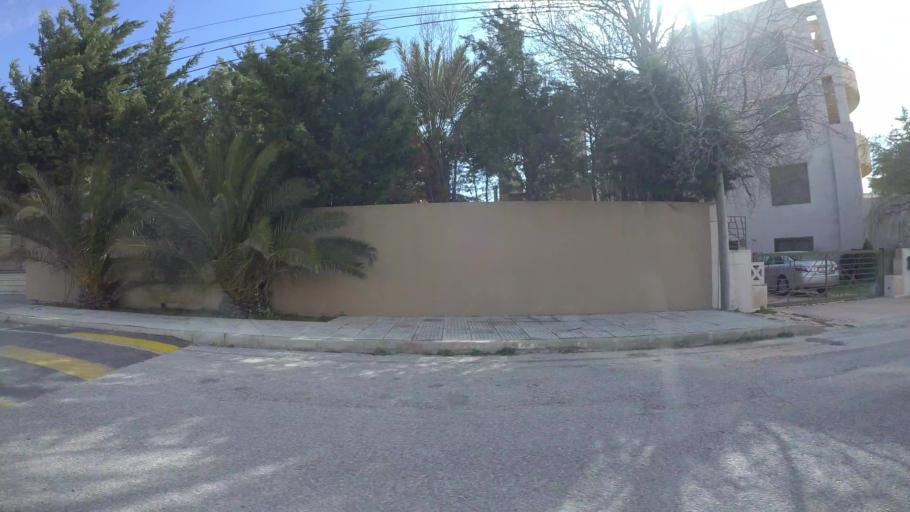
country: JO
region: Amman
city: Al Jubayhah
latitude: 32.0037
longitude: 35.8425
